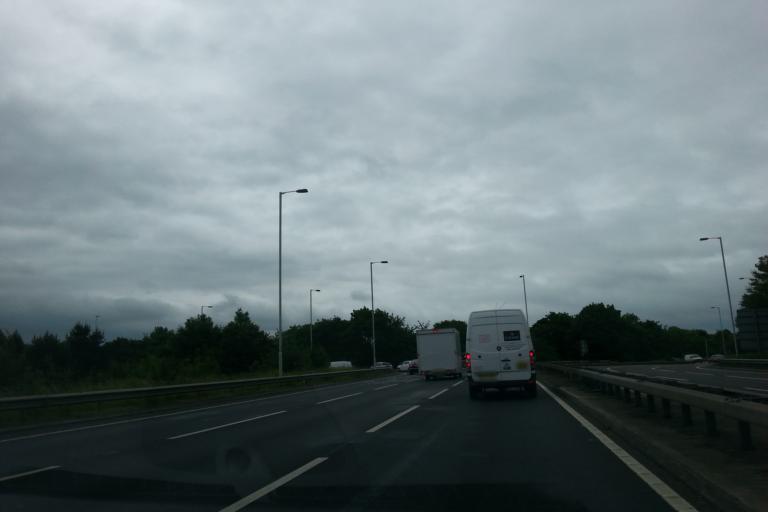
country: GB
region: England
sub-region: Cambridgeshire
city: Yaxley
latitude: 52.5473
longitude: -0.2653
